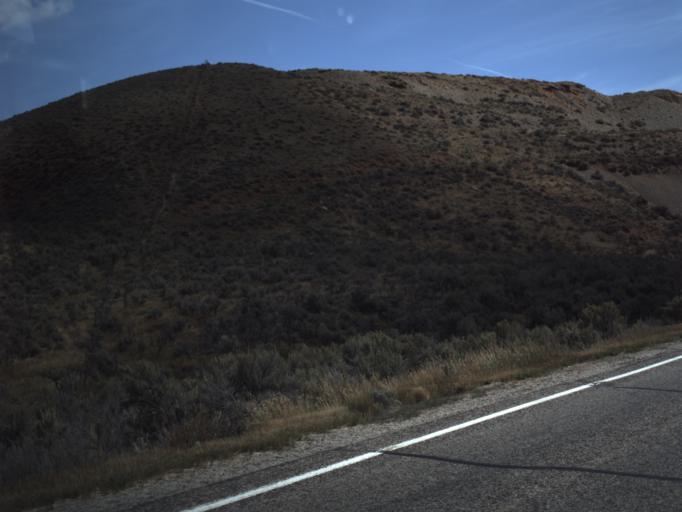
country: US
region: Utah
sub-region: Rich County
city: Randolph
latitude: 41.7807
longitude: -111.1981
